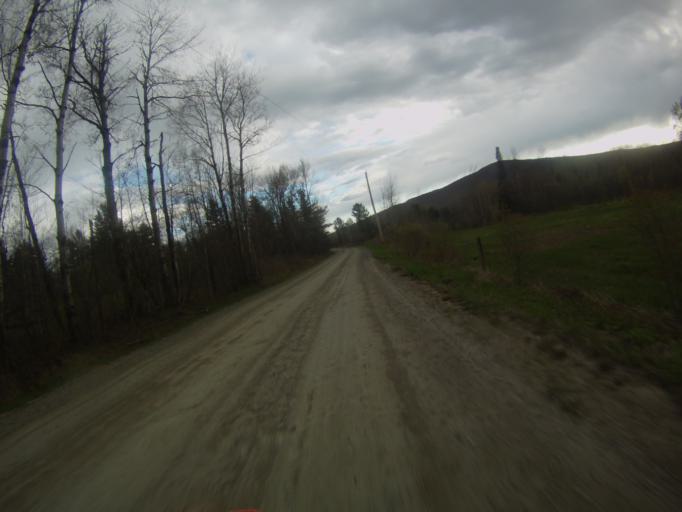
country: US
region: Vermont
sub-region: Addison County
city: Bristol
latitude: 44.0392
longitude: -73.0151
